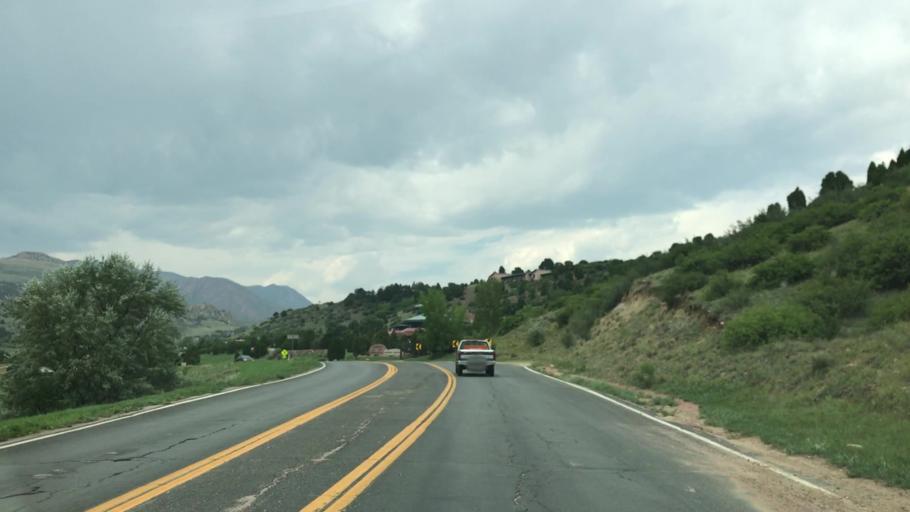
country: US
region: Colorado
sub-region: El Paso County
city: Manitou Springs
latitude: 38.8759
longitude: -104.8693
